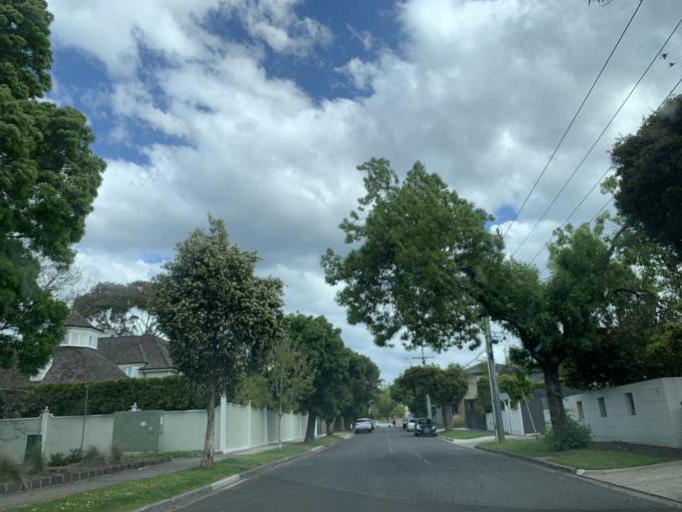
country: AU
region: Victoria
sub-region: Bayside
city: Hampton
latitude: -37.9247
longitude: 145.0009
